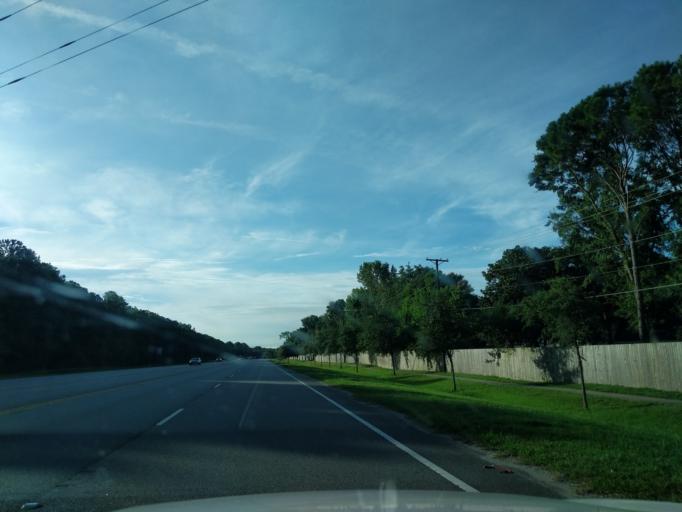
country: US
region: South Carolina
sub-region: Charleston County
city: Isle of Palms
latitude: 32.8286
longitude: -79.8215
